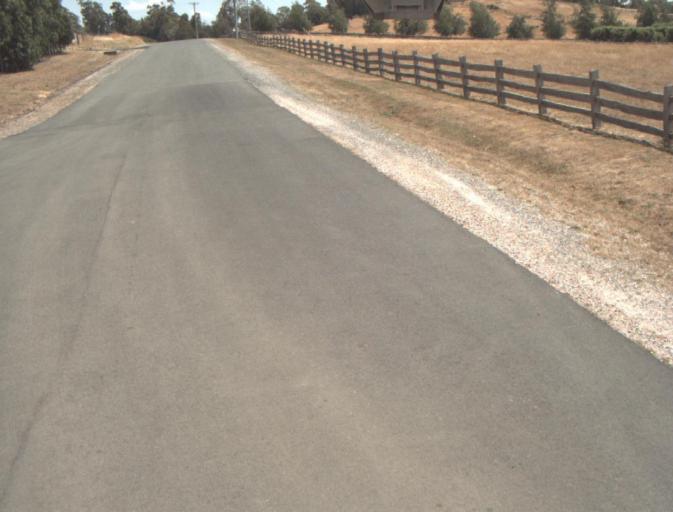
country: AU
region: Tasmania
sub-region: Launceston
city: Newstead
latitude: -41.4954
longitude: 147.2156
